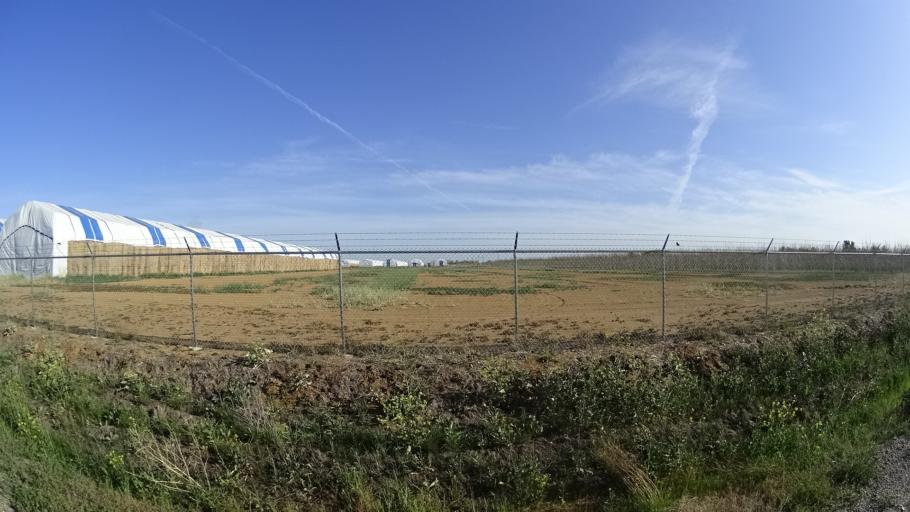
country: US
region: California
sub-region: Glenn County
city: Willows
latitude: 39.5099
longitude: -122.2341
